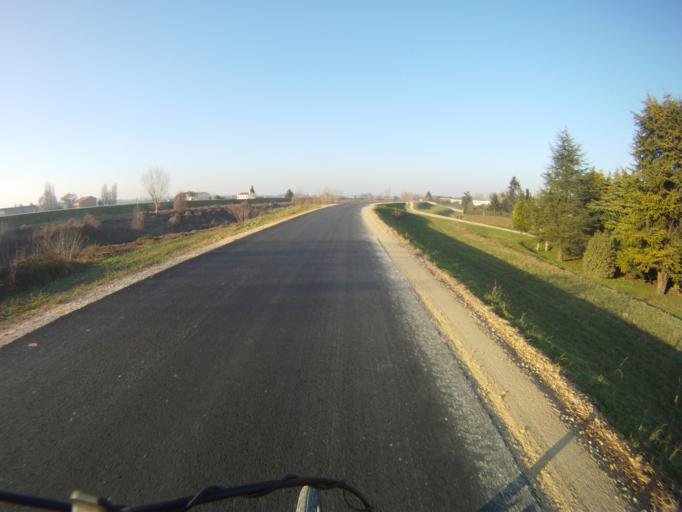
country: IT
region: Veneto
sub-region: Provincia di Padova
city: Legnaro
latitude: 45.3327
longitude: 11.9381
